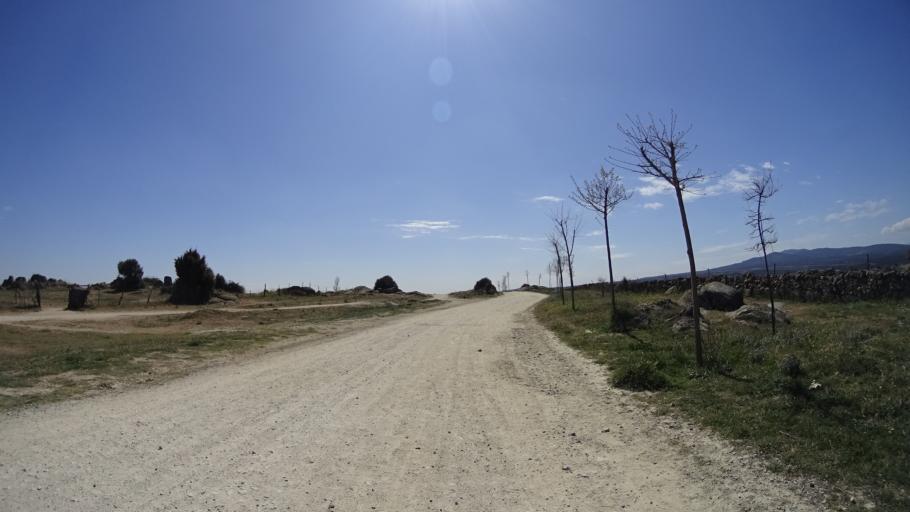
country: ES
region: Madrid
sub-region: Provincia de Madrid
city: Colmenar Viejo
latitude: 40.6616
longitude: -3.7883
